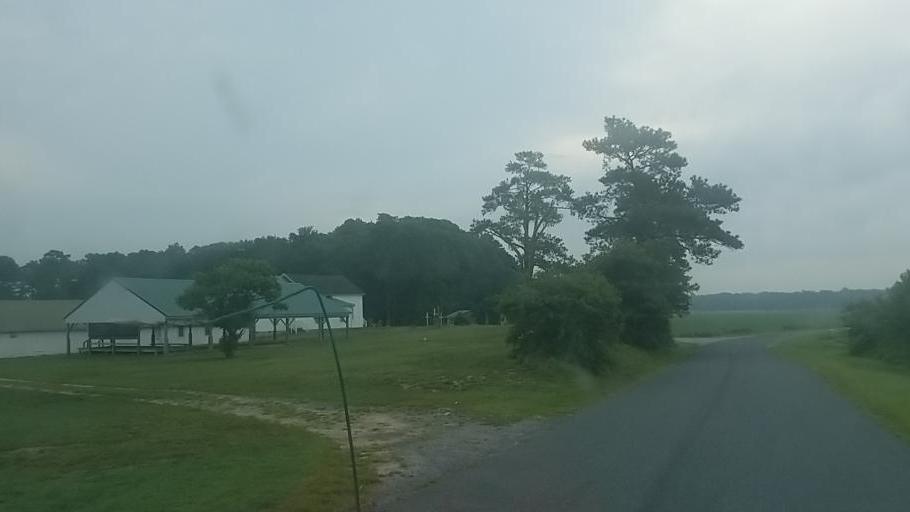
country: US
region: Maryland
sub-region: Wicomico County
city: Pittsville
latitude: 38.4521
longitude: -75.3568
